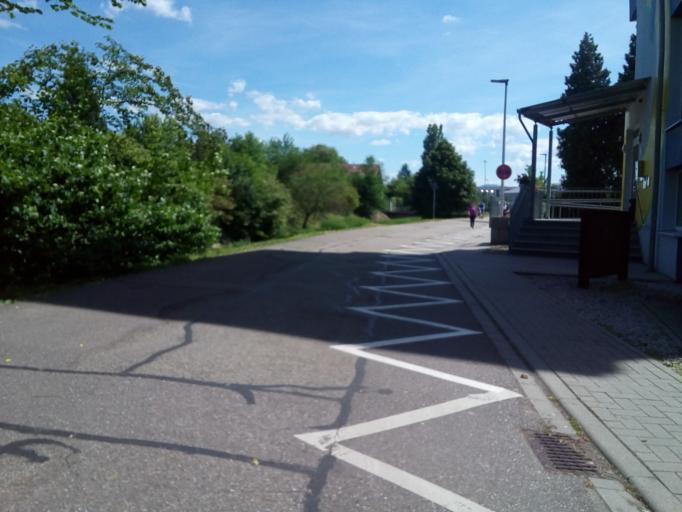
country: DE
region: Baden-Wuerttemberg
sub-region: Freiburg Region
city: Renchen
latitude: 48.5810
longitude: 8.0122
